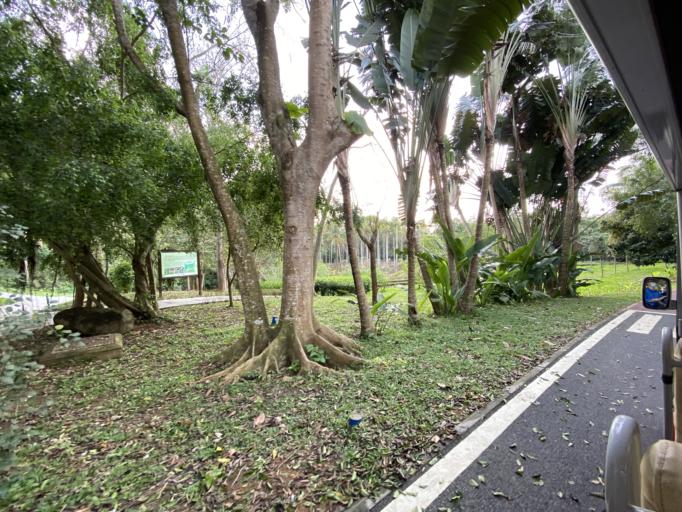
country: CN
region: Hainan
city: Nanqiao
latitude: 18.7318
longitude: 110.1910
